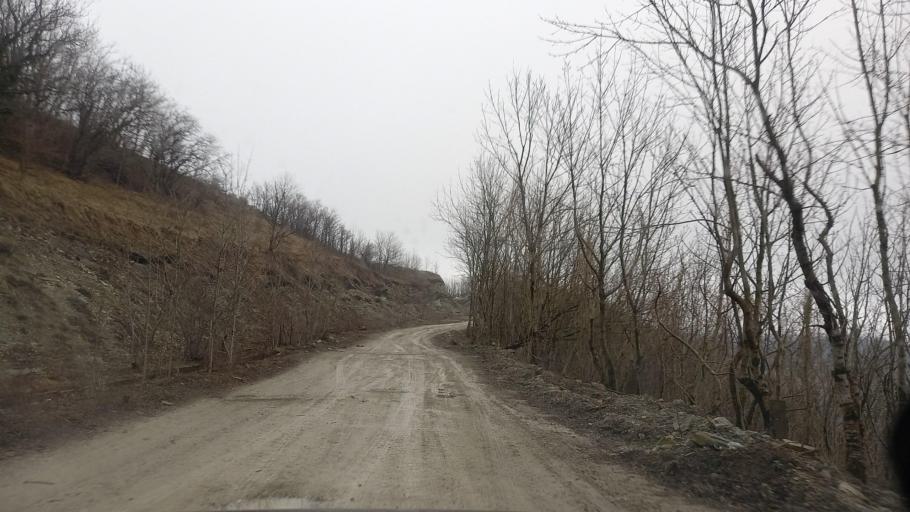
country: RU
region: Krasnodarskiy
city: Divnomorskoye
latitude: 44.5875
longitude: 38.2531
